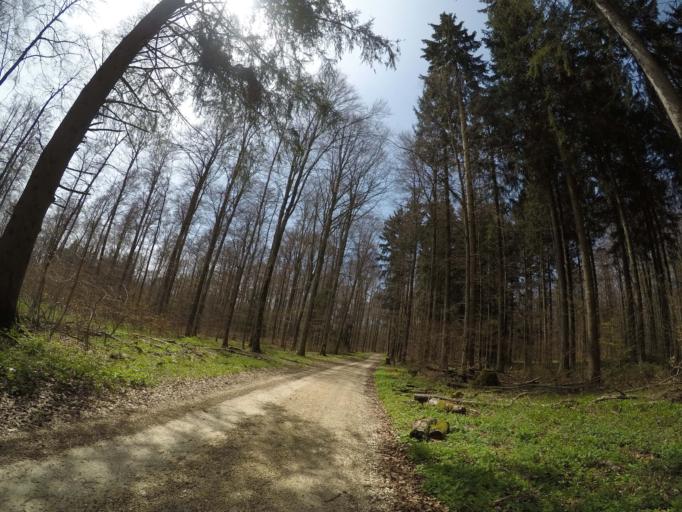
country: DE
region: Baden-Wuerttemberg
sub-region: Regierungsbezirk Stuttgart
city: Neidlingen
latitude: 48.5383
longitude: 9.5732
